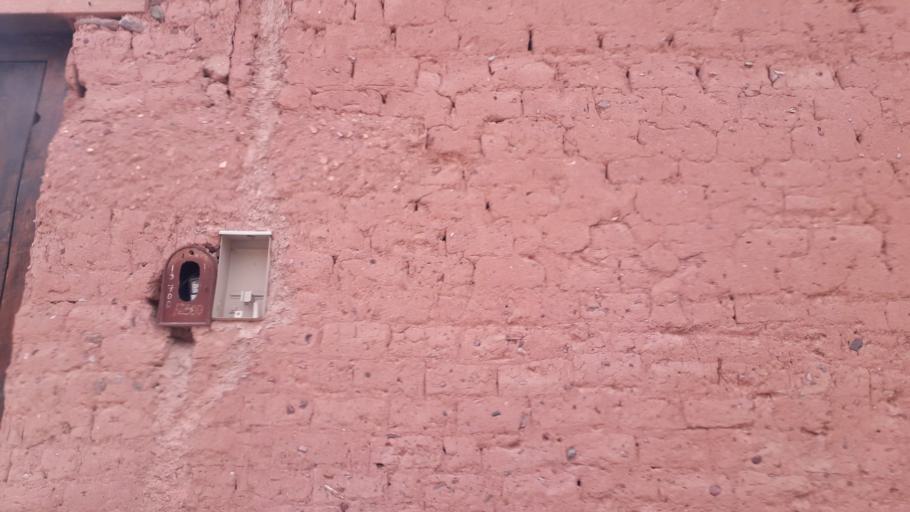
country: AR
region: Jujuy
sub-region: Departamento de Humahuaca
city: Humahuaca
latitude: -23.3040
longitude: -65.3557
